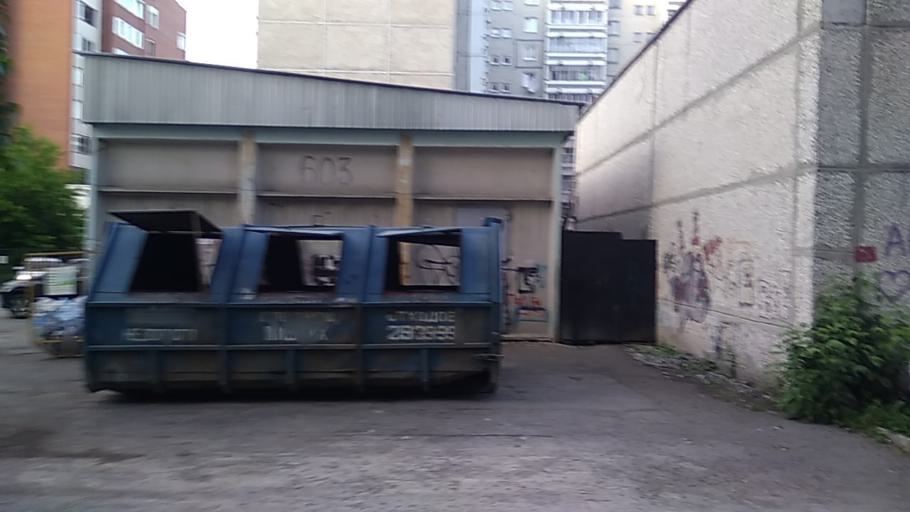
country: RU
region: Sverdlovsk
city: Yekaterinburg
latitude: 56.8087
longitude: 60.5993
